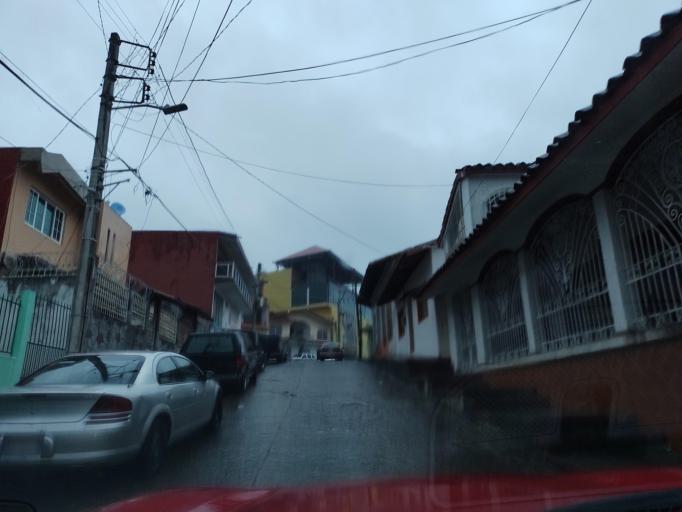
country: MX
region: Veracruz
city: Papantla de Olarte
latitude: 20.4480
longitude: -97.3264
